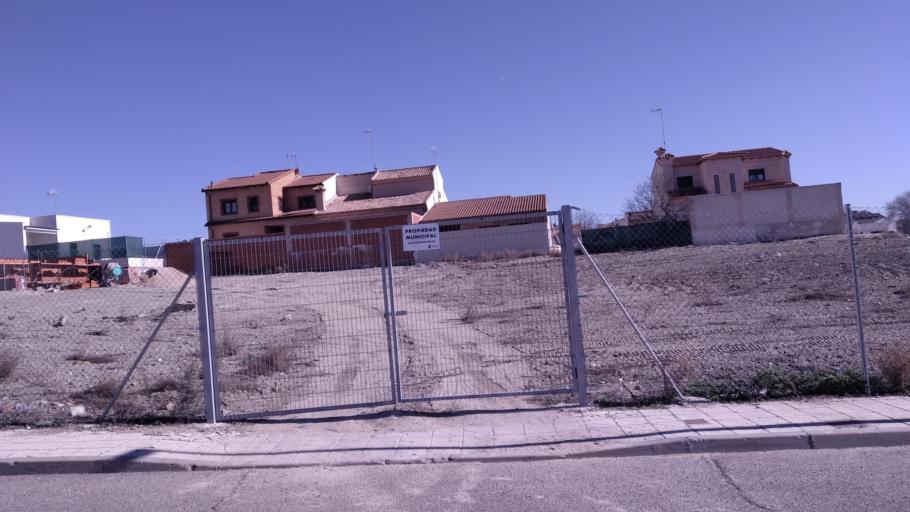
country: ES
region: Castille-La Mancha
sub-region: Province of Toledo
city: Esquivias
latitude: 40.1041
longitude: -3.7761
